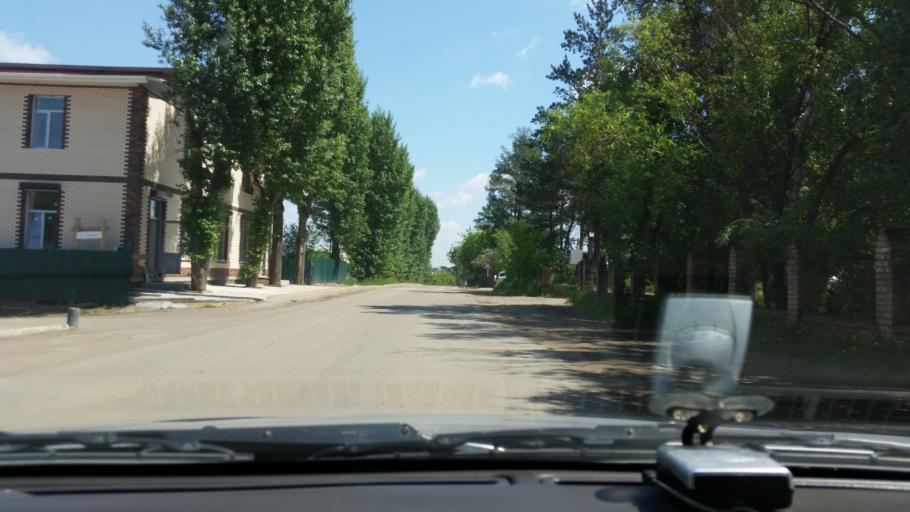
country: RU
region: Irkutsk
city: Dzerzhinsk
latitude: 52.2811
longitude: 104.3829
